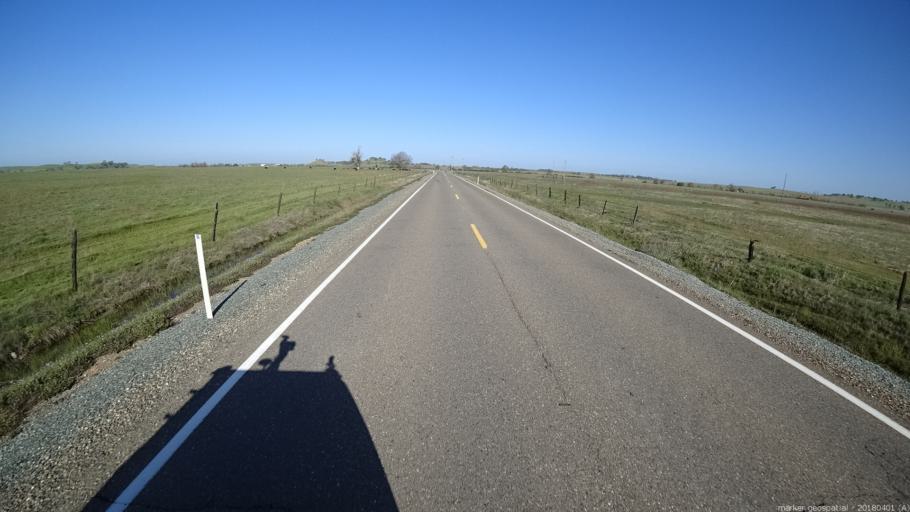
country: US
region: California
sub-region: Sacramento County
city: Rancho Murieta
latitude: 38.4191
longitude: -121.0426
